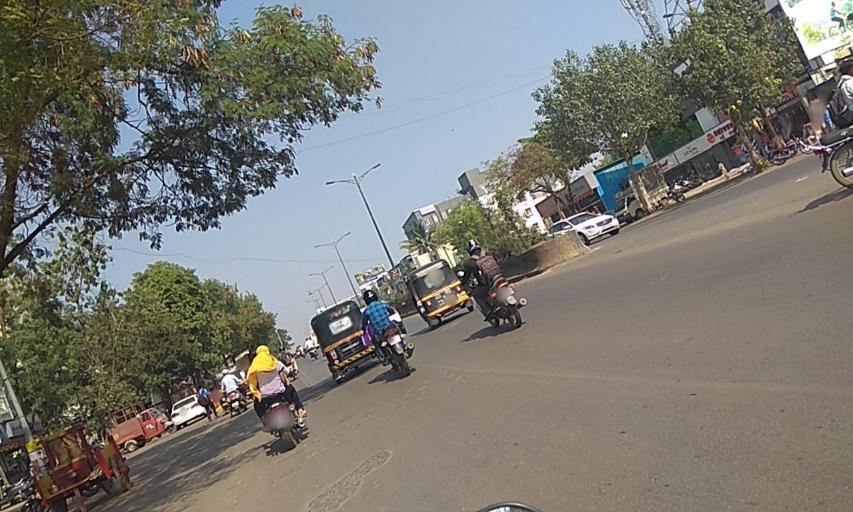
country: IN
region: Maharashtra
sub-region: Pune Division
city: Lohogaon
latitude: 18.5382
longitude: 73.9342
